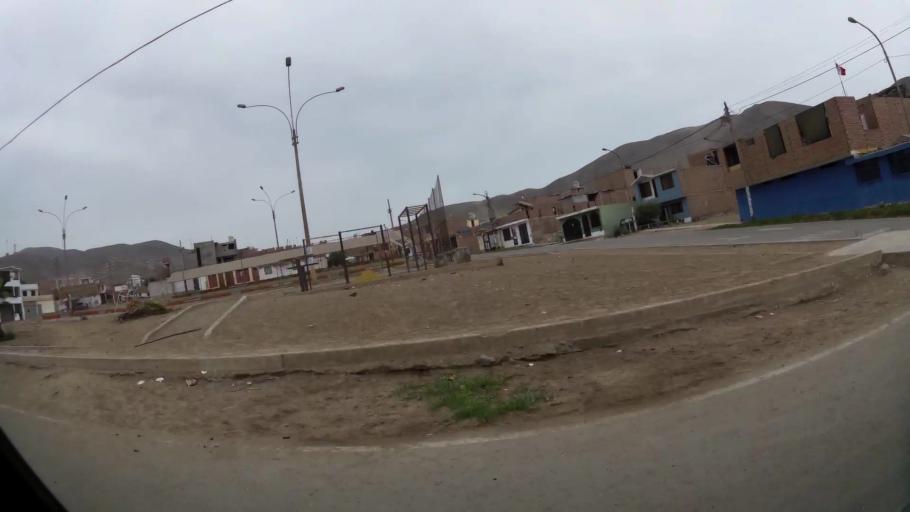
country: PE
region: Lima
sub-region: Lima
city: Santa Rosa
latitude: -11.7892
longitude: -77.1572
